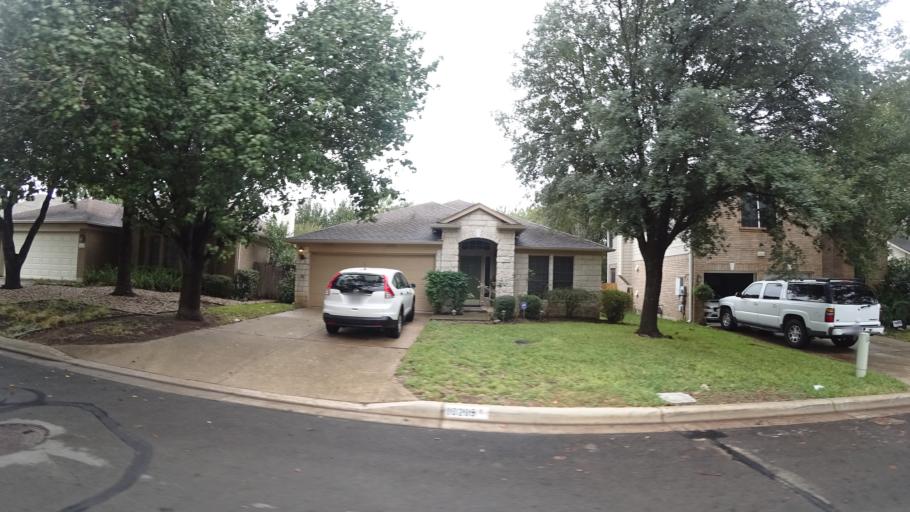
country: US
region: Texas
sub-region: Travis County
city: Shady Hollow
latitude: 30.1885
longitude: -97.8670
